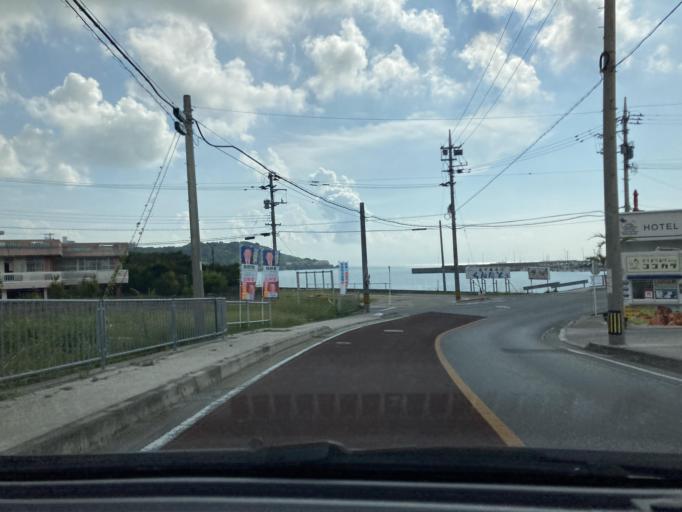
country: JP
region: Okinawa
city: Itoman
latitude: 26.1334
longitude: 127.7715
